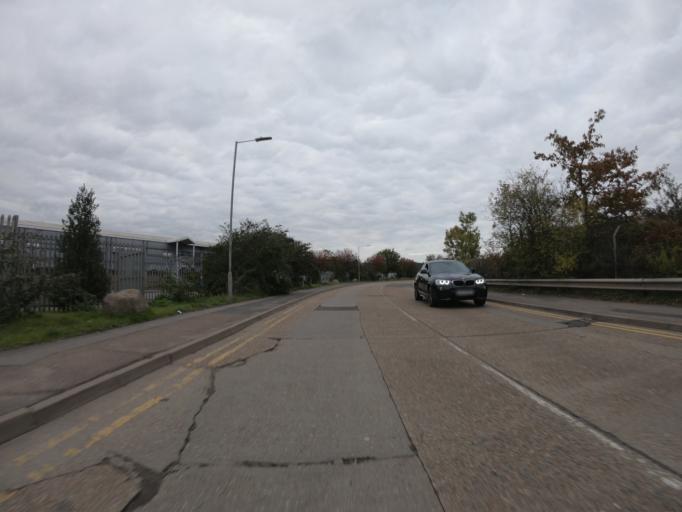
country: GB
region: England
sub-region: Kent
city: West Thurrock
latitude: 51.4800
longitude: 0.2689
